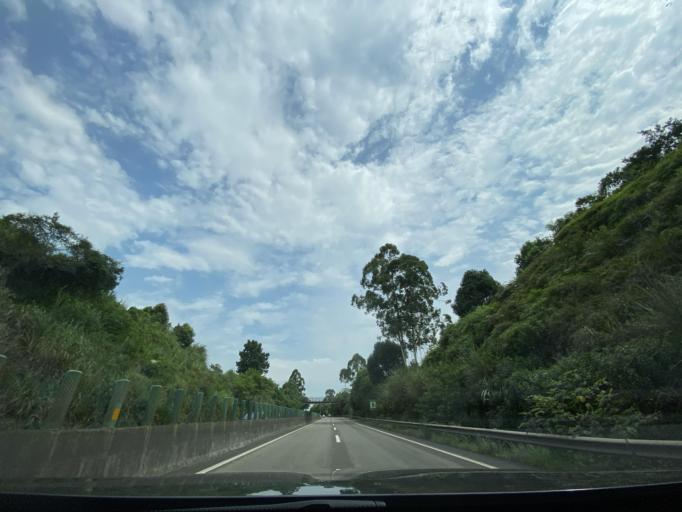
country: CN
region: Sichuan
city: Chonglong
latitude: 29.7939
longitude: 104.7251
